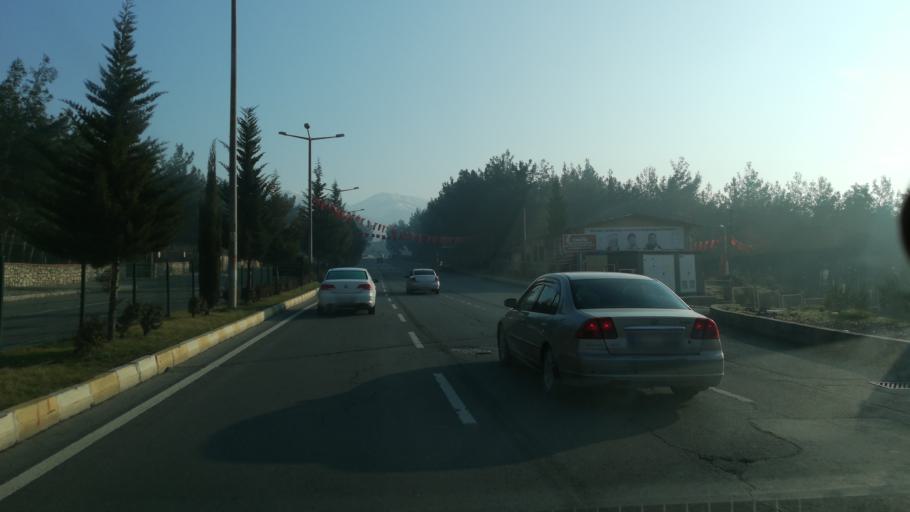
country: TR
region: Kahramanmaras
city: Kahramanmaras
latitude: 37.5976
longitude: 36.9196
